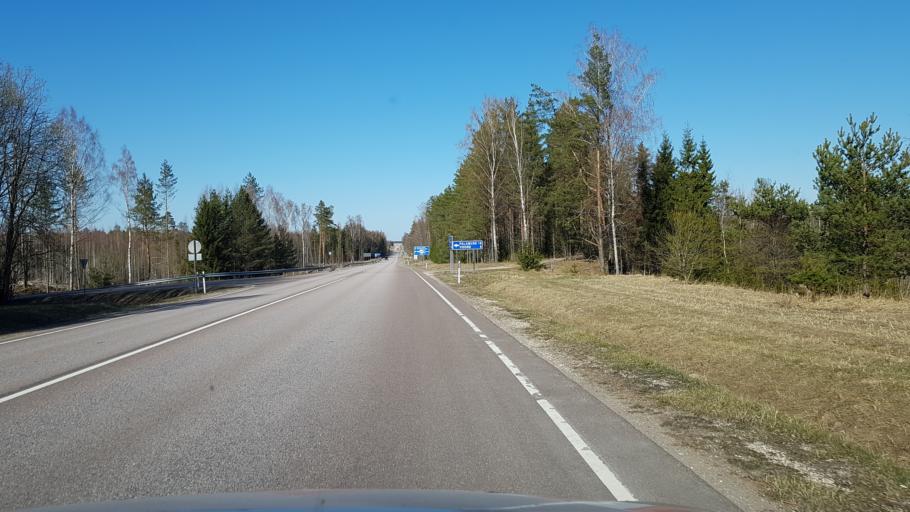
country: EE
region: Jogevamaa
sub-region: Mustvee linn
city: Mustvee
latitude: 58.7285
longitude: 26.8386
